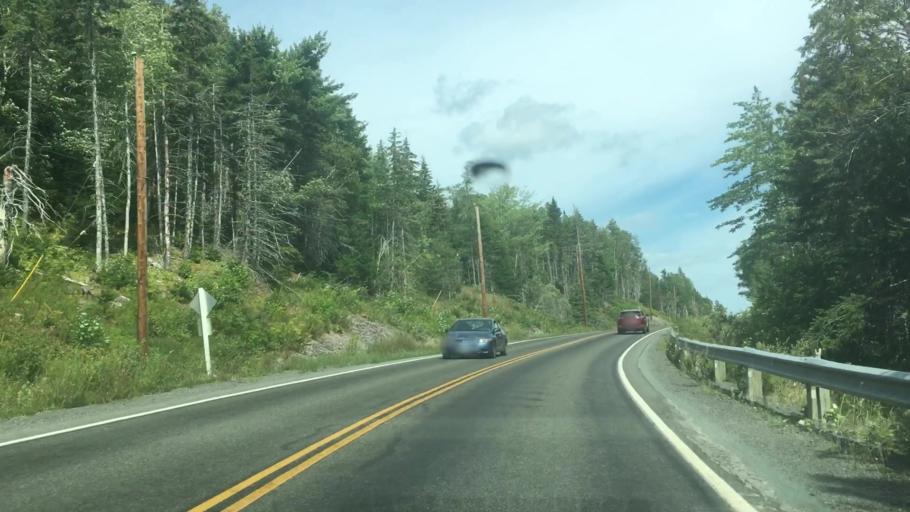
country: CA
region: Nova Scotia
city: Sydney Mines
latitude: 46.2081
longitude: -60.6227
